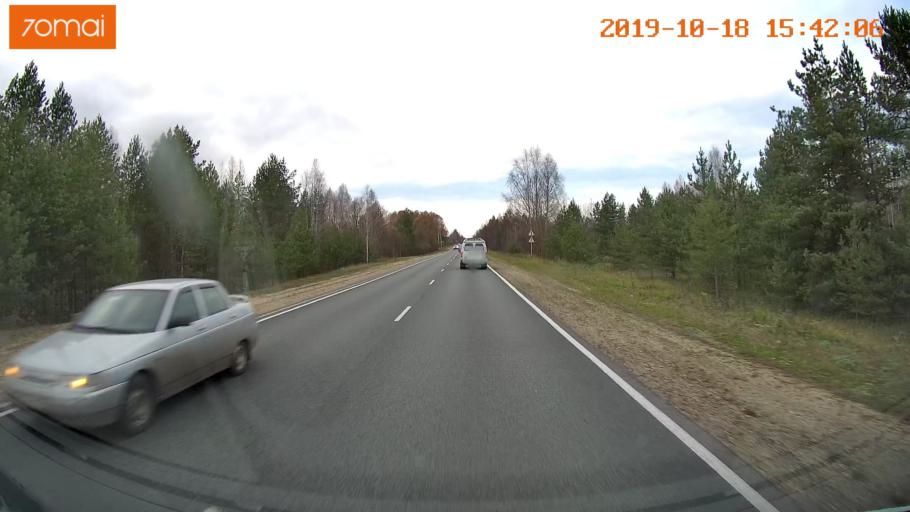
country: RU
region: Vladimir
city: Golovino
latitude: 55.9521
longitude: 40.5730
